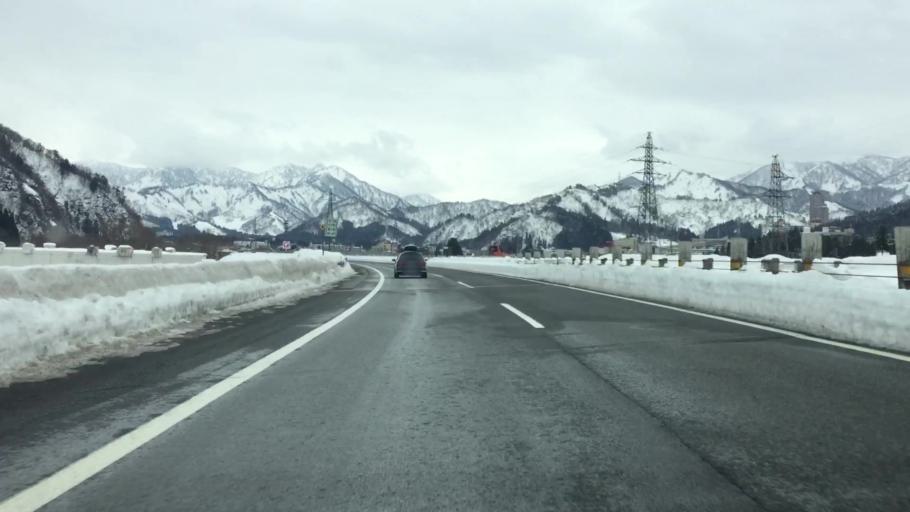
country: JP
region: Niigata
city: Shiozawa
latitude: 36.9486
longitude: 138.8037
